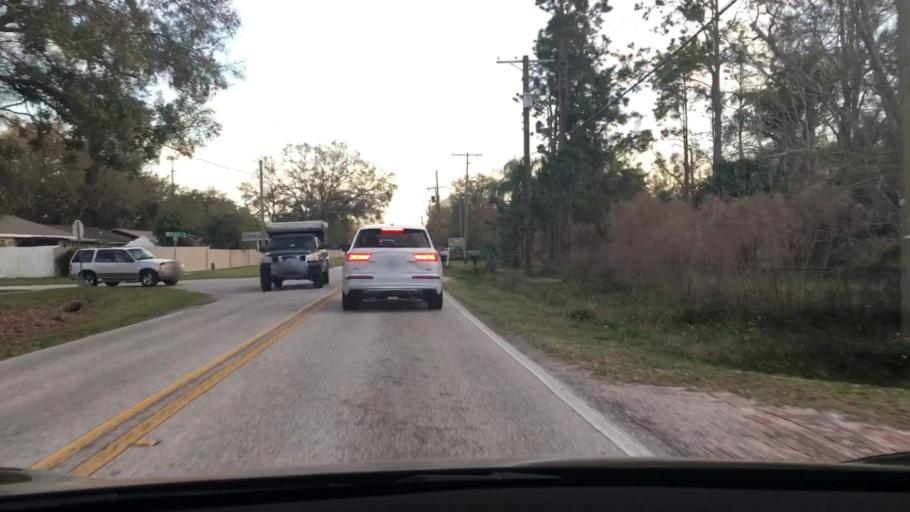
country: US
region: Florida
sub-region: Hillsborough County
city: Greater Northdale
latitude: 28.0898
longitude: -82.5399
